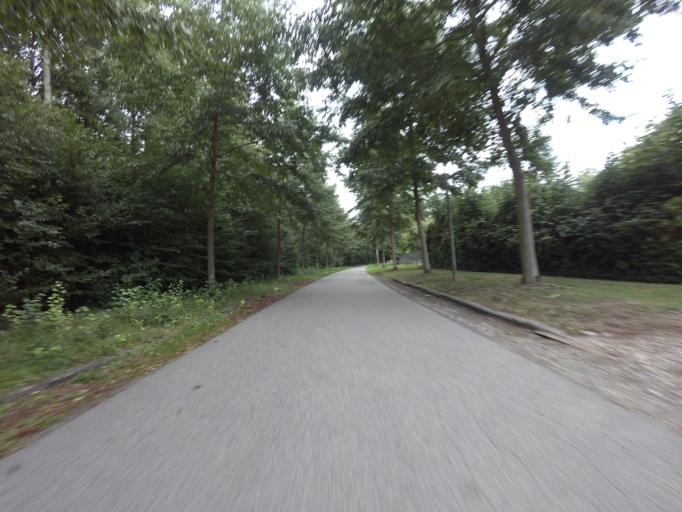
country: BE
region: Flanders
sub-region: Provincie Vlaams-Brabant
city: Kampenhout
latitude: 50.9295
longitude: 4.5533
